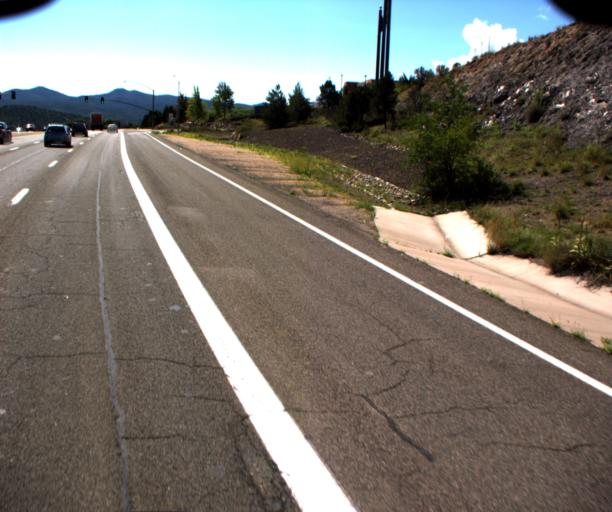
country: US
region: Arizona
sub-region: Yavapai County
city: Prescott
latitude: 34.5509
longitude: -112.4082
